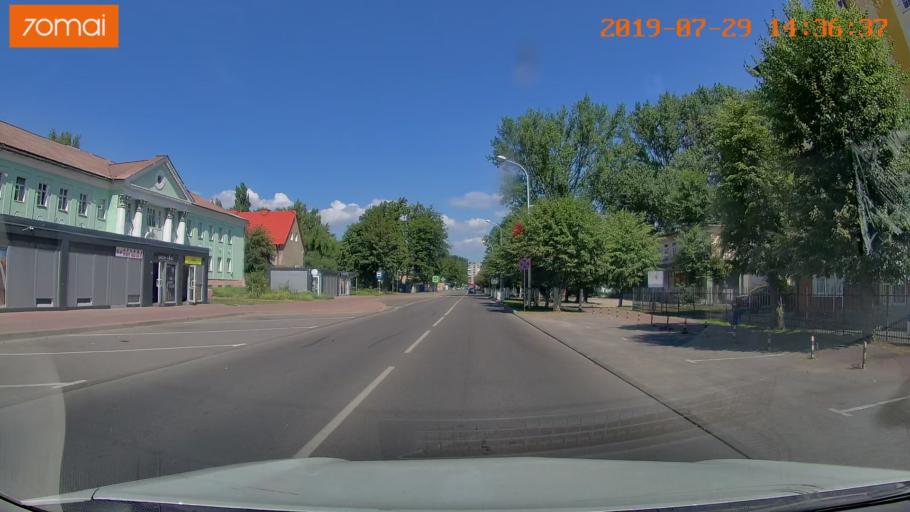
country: RU
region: Kaliningrad
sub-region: Gorod Kaliningrad
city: Baltiysk
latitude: 54.6479
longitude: 19.9015
